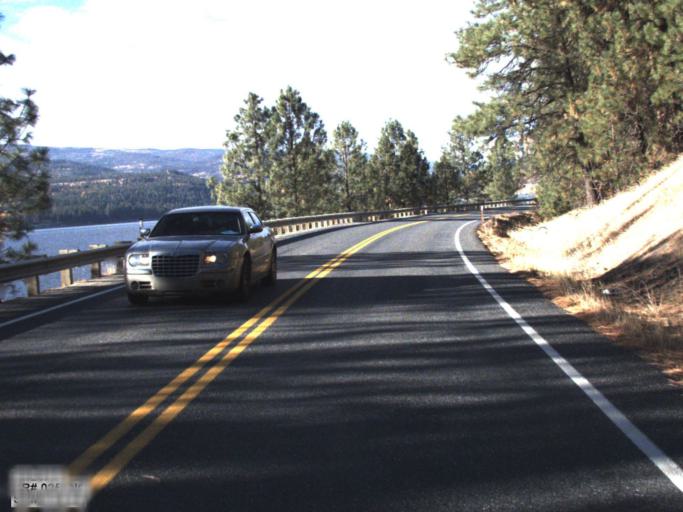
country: US
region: Washington
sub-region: Stevens County
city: Kettle Falls
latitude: 48.6497
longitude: -118.0834
